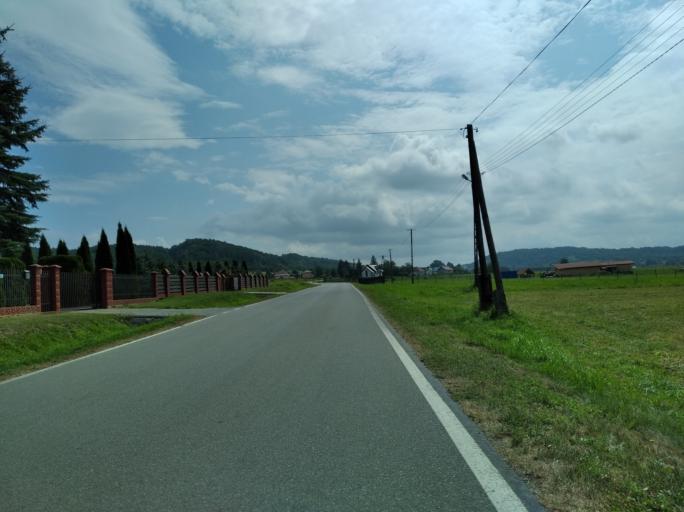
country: PL
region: Subcarpathian Voivodeship
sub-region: Powiat krosnienski
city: Wojaszowka
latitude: 49.7971
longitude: 21.6793
